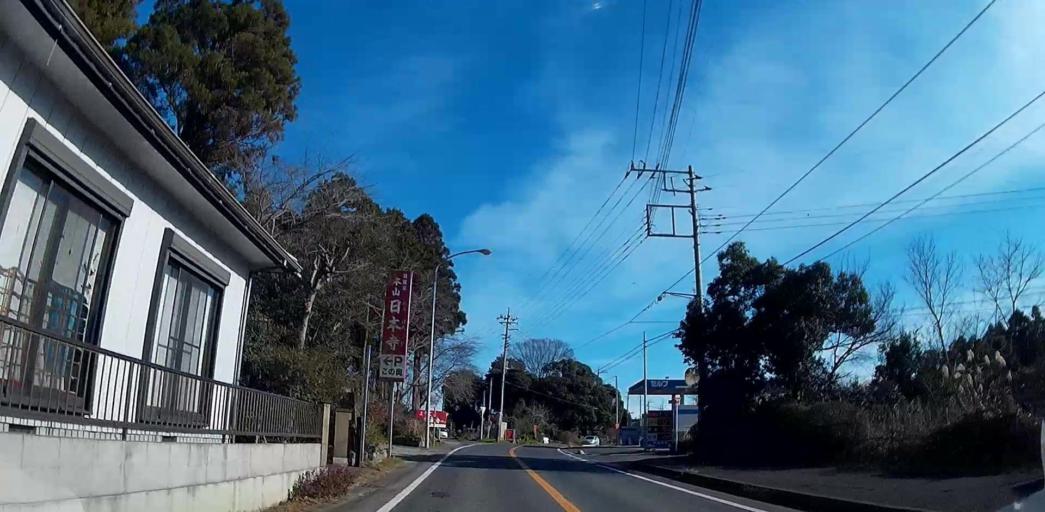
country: JP
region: Chiba
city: Yokaichiba
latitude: 35.7375
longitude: 140.4864
